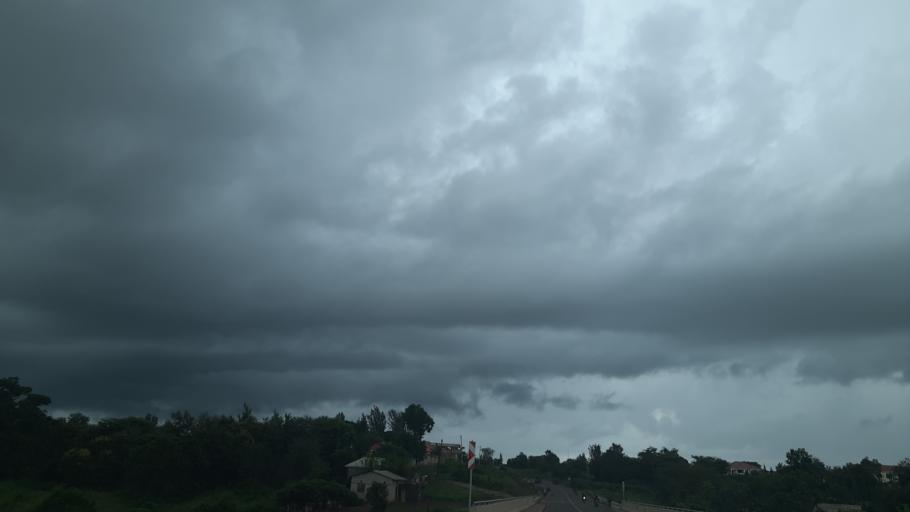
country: TZ
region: Arusha
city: Arusha
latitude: -3.4451
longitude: 36.7014
